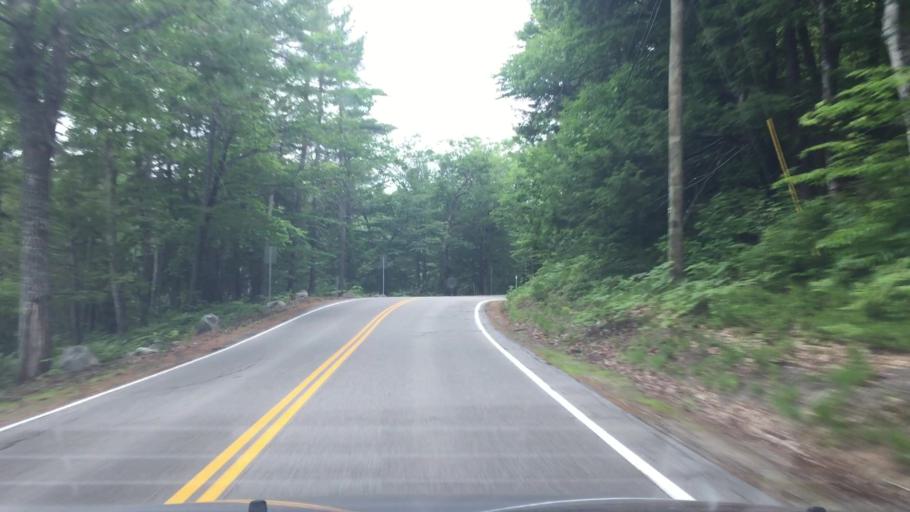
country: US
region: New Hampshire
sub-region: Carroll County
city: Madison
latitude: 43.8850
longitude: -71.0770
